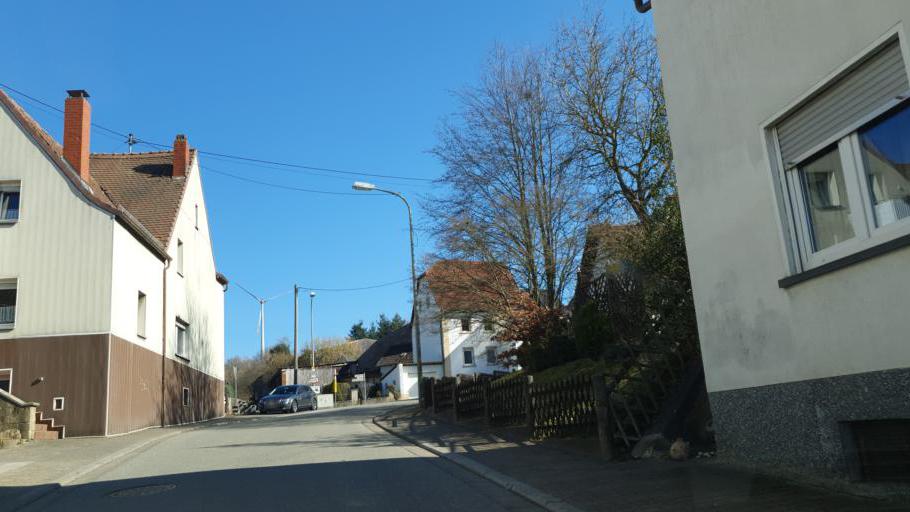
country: DE
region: Rheinland-Pfalz
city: Schellweiler
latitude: 49.5150
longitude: 7.3921
